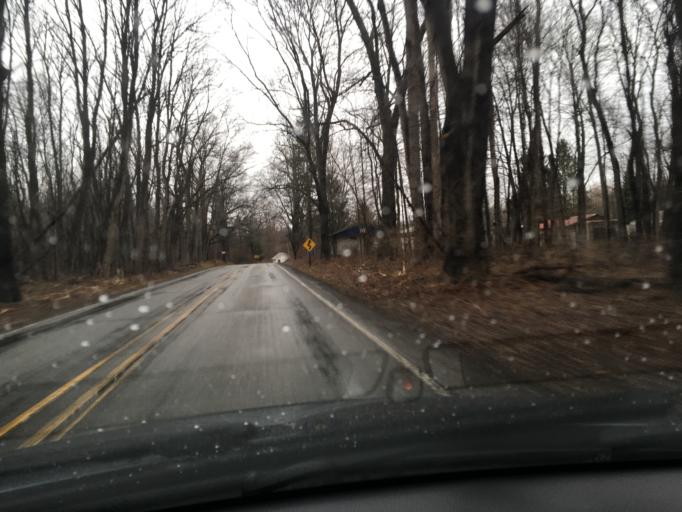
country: US
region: Michigan
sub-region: Jackson County
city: Grass Lake
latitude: 42.3276
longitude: -84.1557
